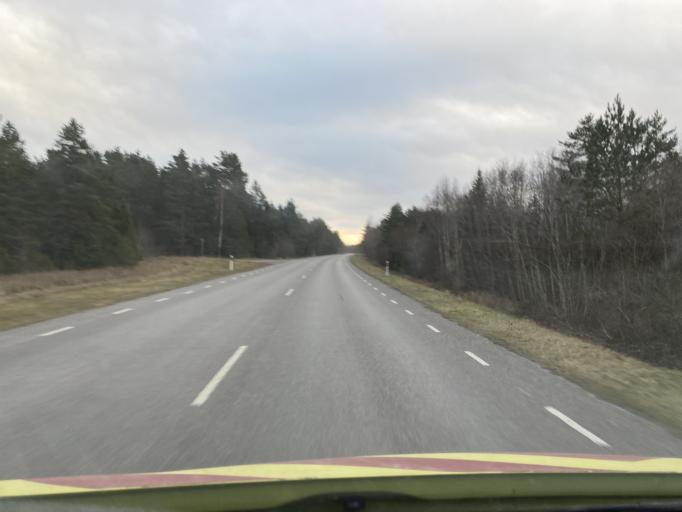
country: EE
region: Laeaene
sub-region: Lihula vald
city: Lihula
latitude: 58.7997
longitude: 23.8569
